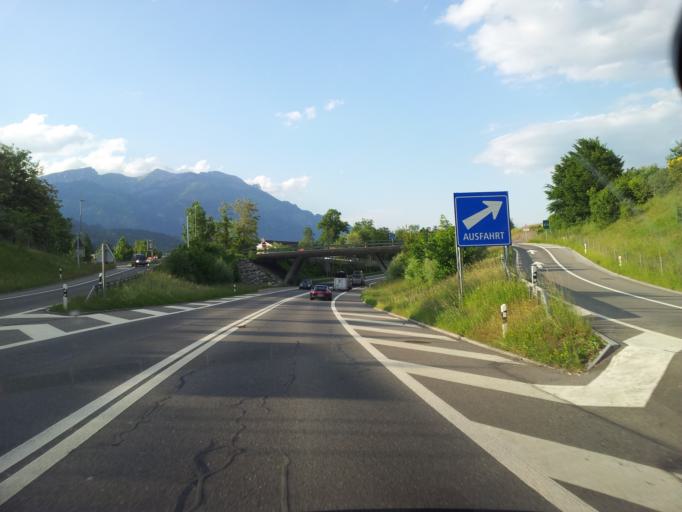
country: CH
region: Obwalden
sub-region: Obwalden
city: Sarnen
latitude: 46.8838
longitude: 8.2465
